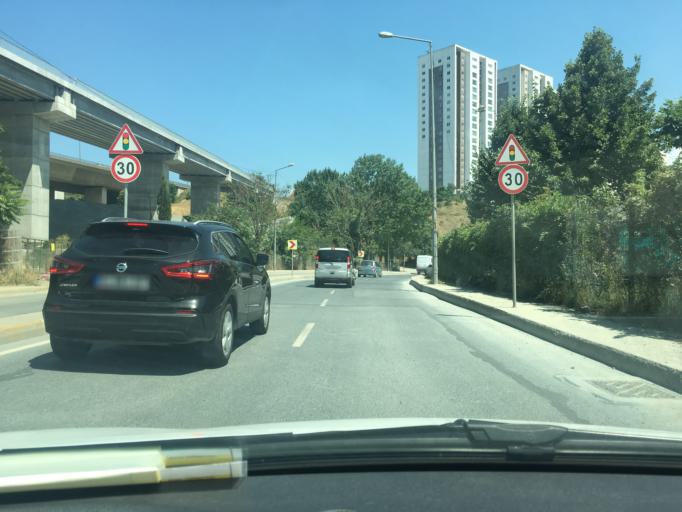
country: TR
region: Istanbul
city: Sisli
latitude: 41.0921
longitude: 28.9327
